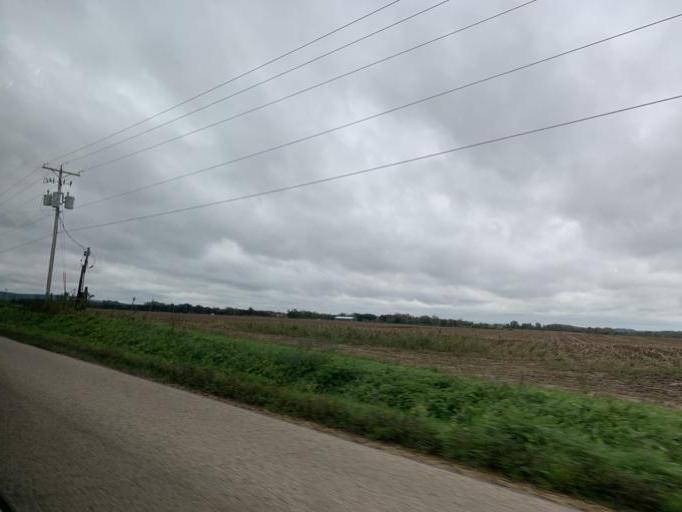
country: US
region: Wisconsin
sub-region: Sauk County
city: Prairie du Sac
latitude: 43.3344
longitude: -89.7692
